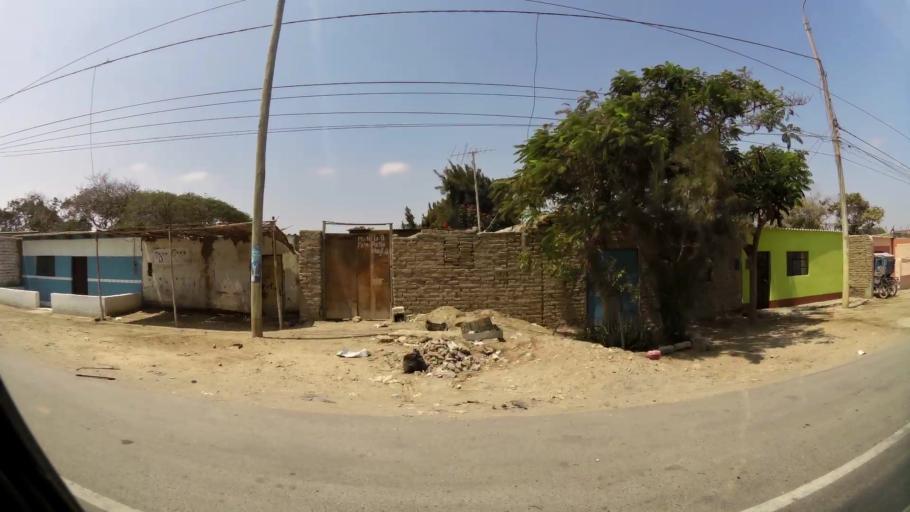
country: PE
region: La Libertad
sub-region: Provincia de Pacasmayo
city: Pacasmayo
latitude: -7.3974
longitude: -79.5579
